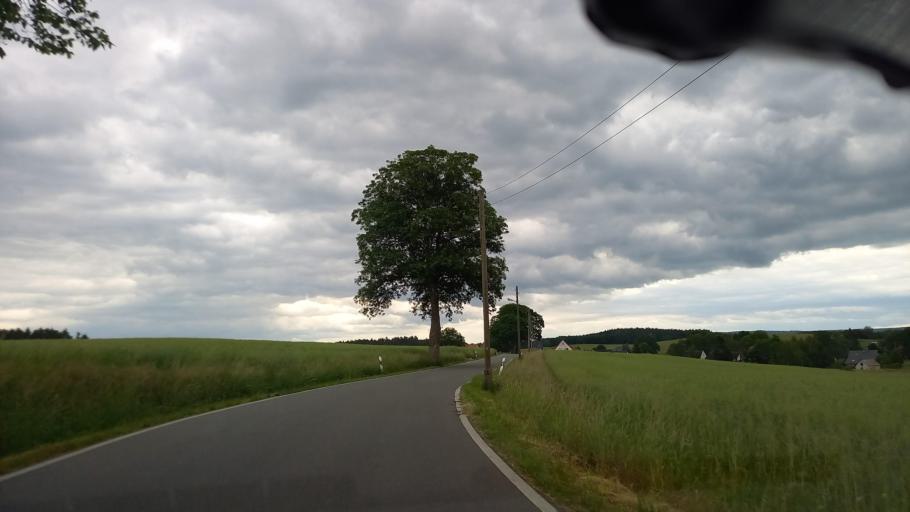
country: DE
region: Saxony
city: Waldkirchen
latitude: 50.6120
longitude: 12.4190
